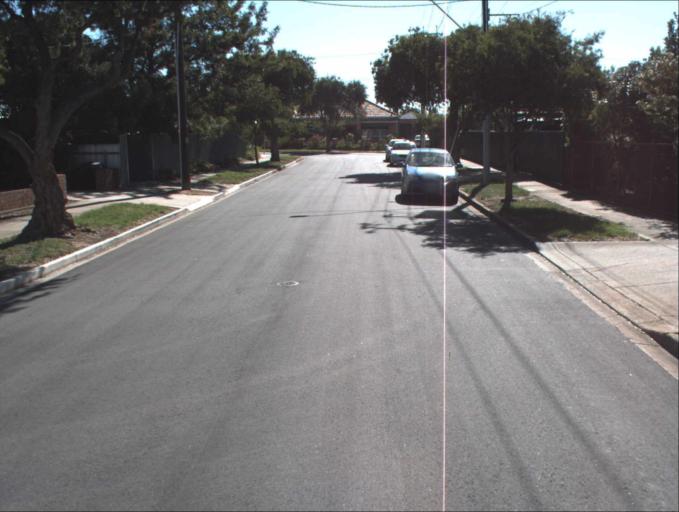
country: AU
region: South Australia
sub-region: Prospect
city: Prospect
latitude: -34.8742
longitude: 138.6077
